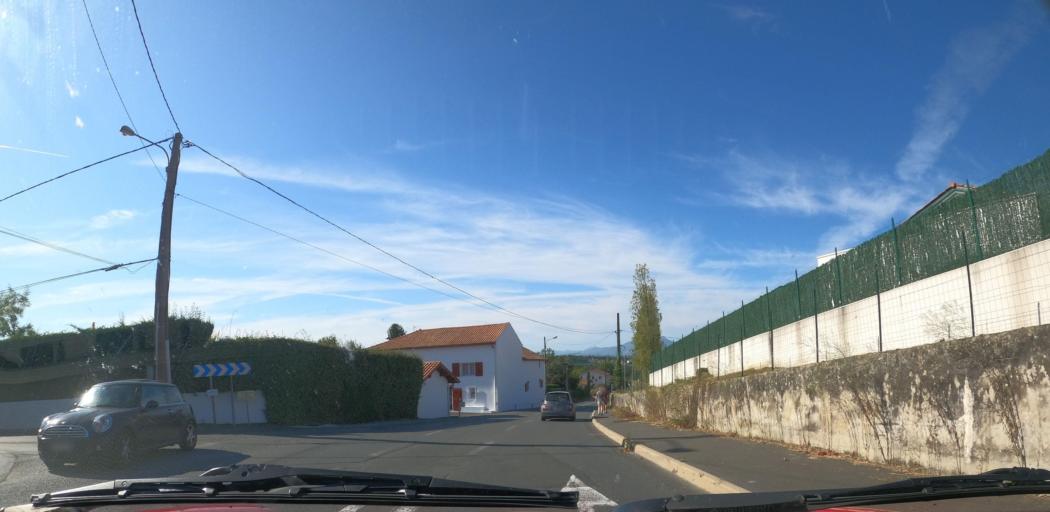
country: FR
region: Aquitaine
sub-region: Departement des Pyrenees-Atlantiques
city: Arbonne
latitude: 43.4440
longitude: -1.5449
